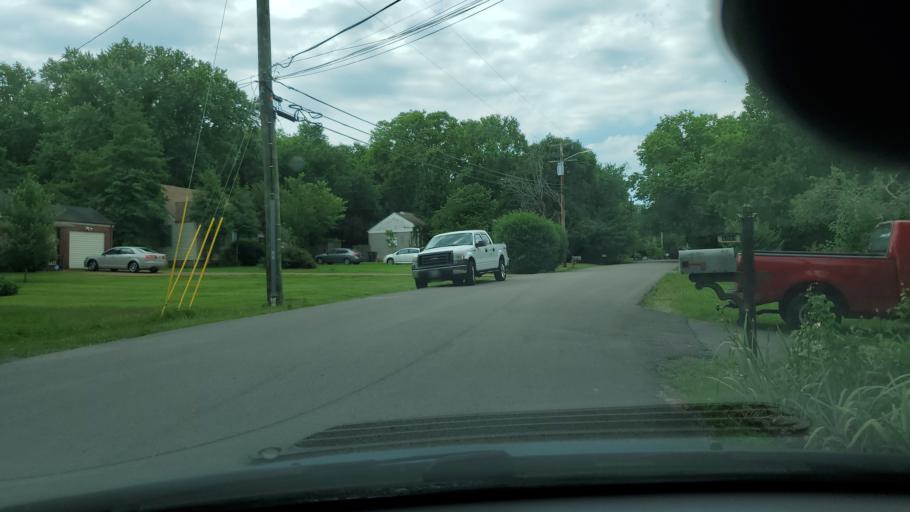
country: US
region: Tennessee
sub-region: Davidson County
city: Lakewood
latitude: 36.2330
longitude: -86.7198
